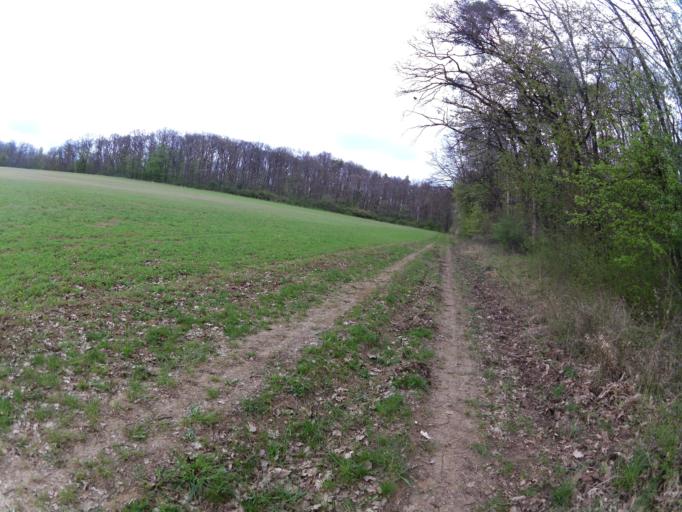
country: DE
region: Bavaria
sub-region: Regierungsbezirk Unterfranken
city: Greussenheim
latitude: 49.8199
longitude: 9.7792
